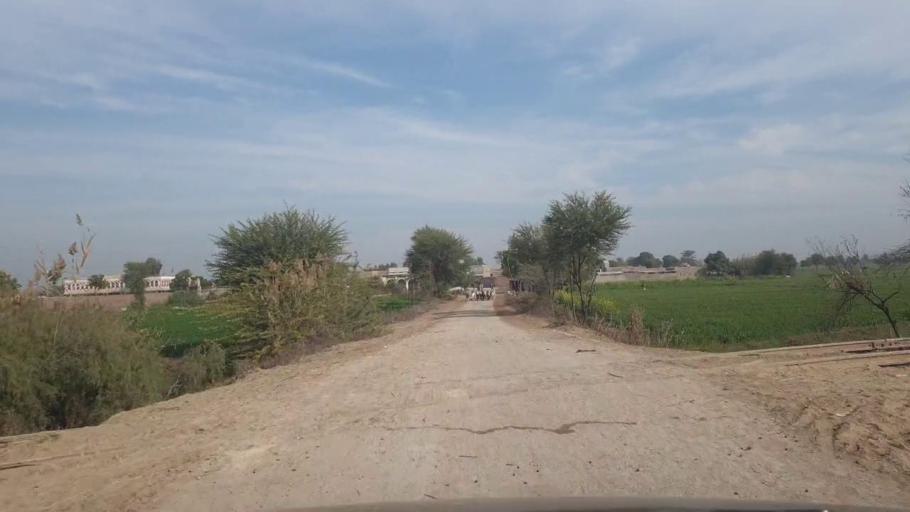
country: PK
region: Sindh
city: Khadro
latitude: 26.1570
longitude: 68.6956
